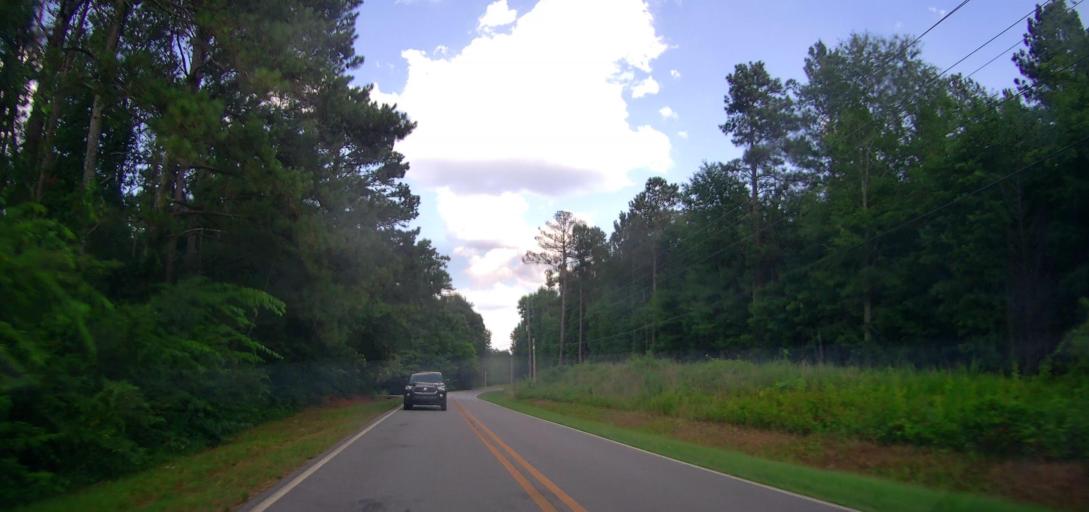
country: US
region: Georgia
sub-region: Henry County
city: Locust Grove
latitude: 33.2235
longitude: -84.1014
